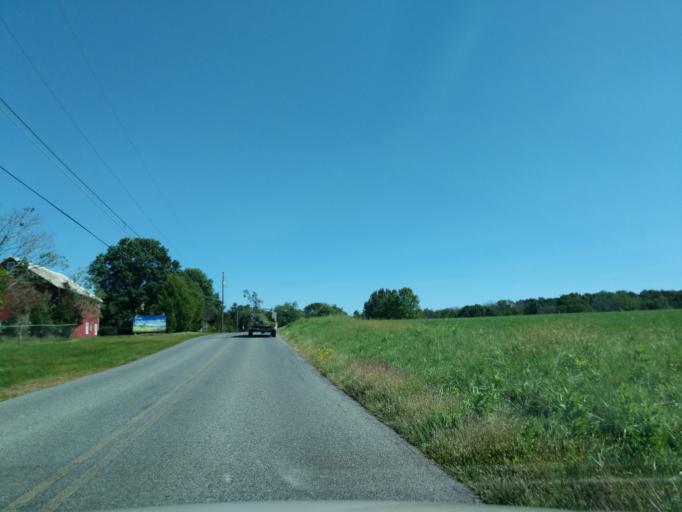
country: US
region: Pennsylvania
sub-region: Montgomery County
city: East Greenville
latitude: 40.4294
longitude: -75.4927
